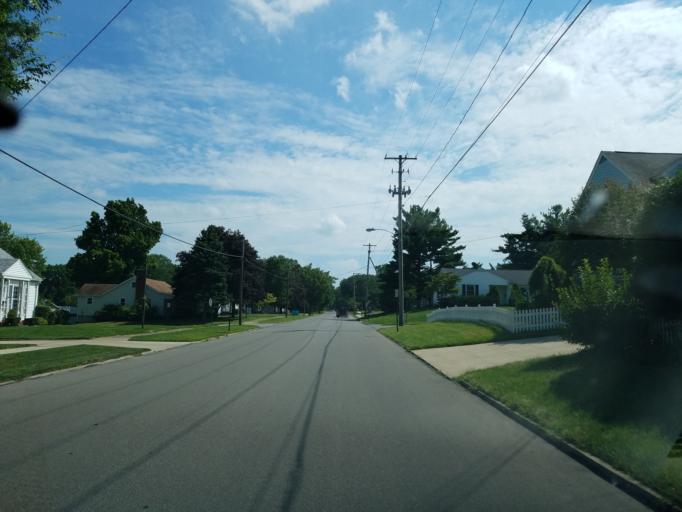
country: US
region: Ohio
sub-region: Ashland County
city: Ashland
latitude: 40.8604
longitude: -82.3079
